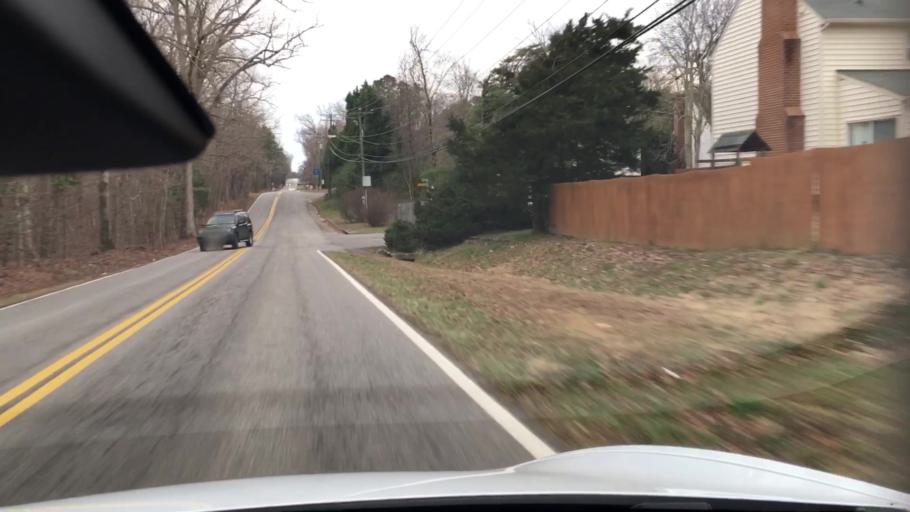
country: US
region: Virginia
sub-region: Chesterfield County
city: Bon Air
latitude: 37.5163
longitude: -77.5755
